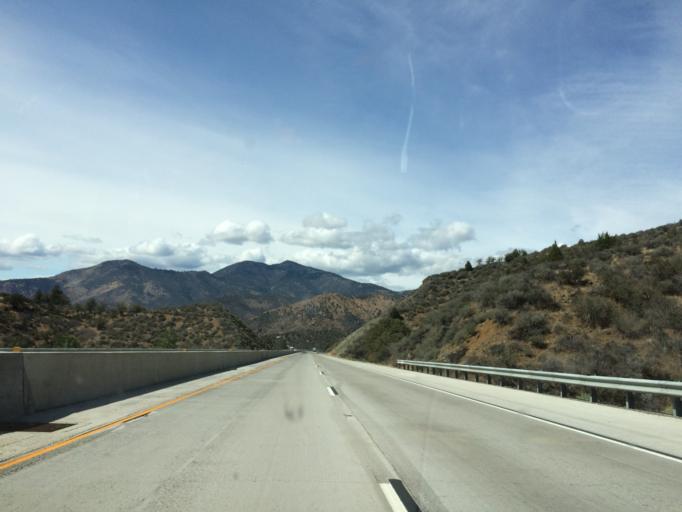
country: US
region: California
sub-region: Siskiyou County
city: Montague
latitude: 41.8135
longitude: -122.5730
